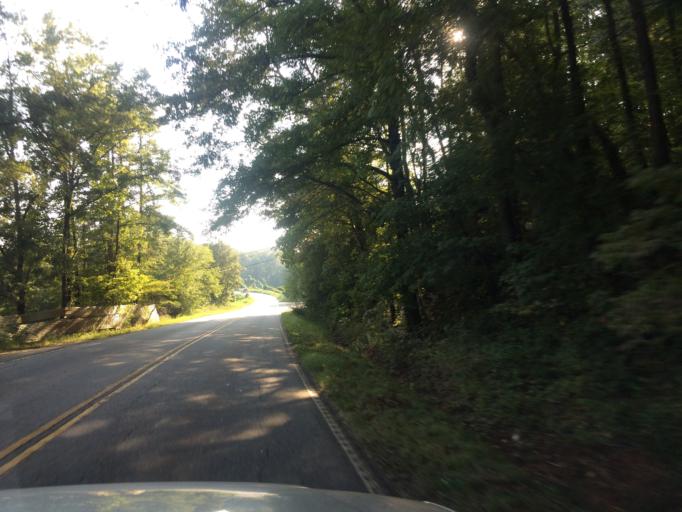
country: US
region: South Carolina
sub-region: Anderson County
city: Piedmont
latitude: 34.6585
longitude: -82.4588
